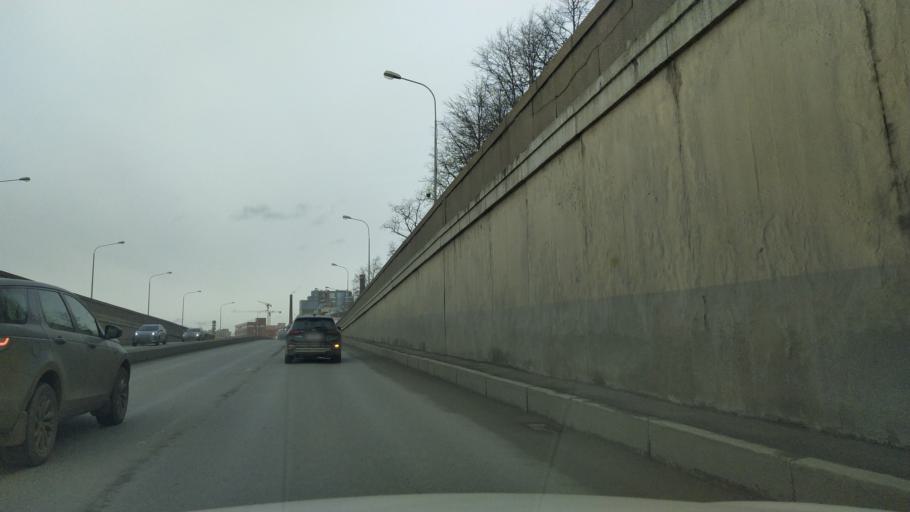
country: RU
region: Leningrad
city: Sampsonievskiy
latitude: 59.9688
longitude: 30.3366
